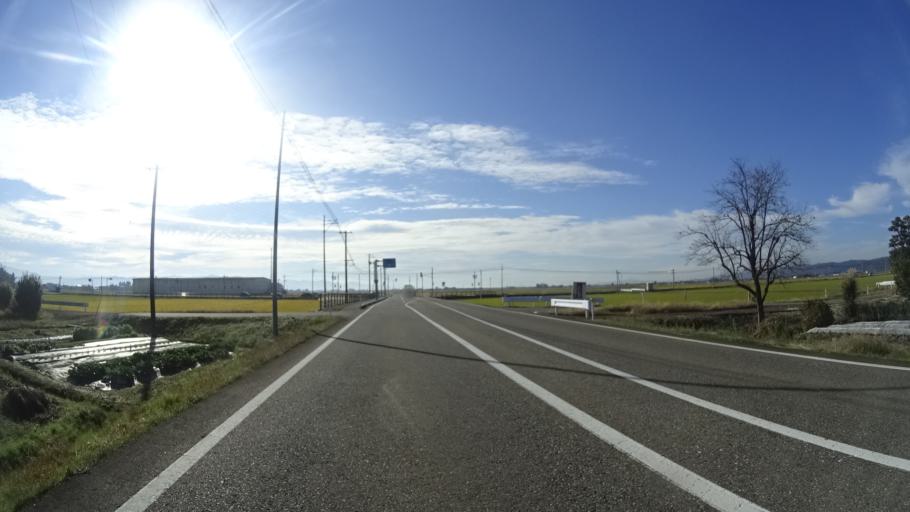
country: JP
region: Niigata
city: Mitsuke
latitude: 37.5564
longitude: 138.8492
